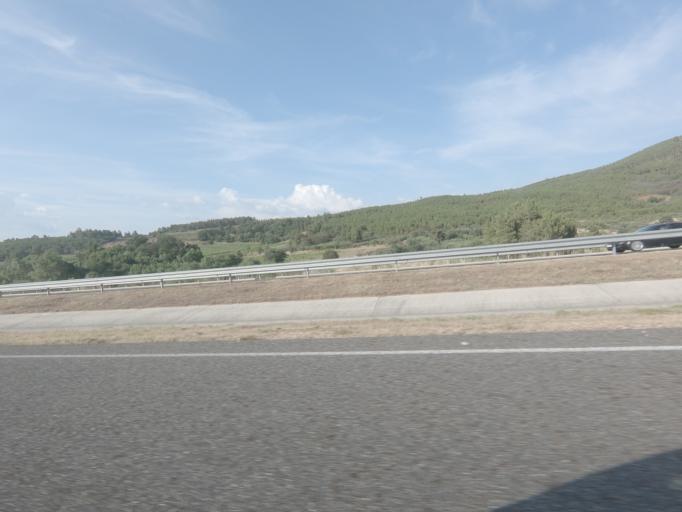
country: ES
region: Galicia
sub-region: Provincia de Ourense
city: Oimbra
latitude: 41.8670
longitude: -7.4316
